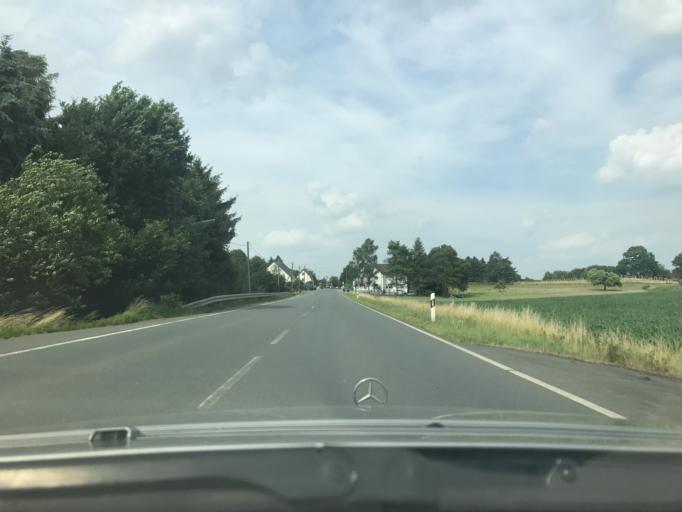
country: DE
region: North Rhine-Westphalia
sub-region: Regierungsbezirk Arnsberg
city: Holzwickede
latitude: 51.4461
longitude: 7.6735
